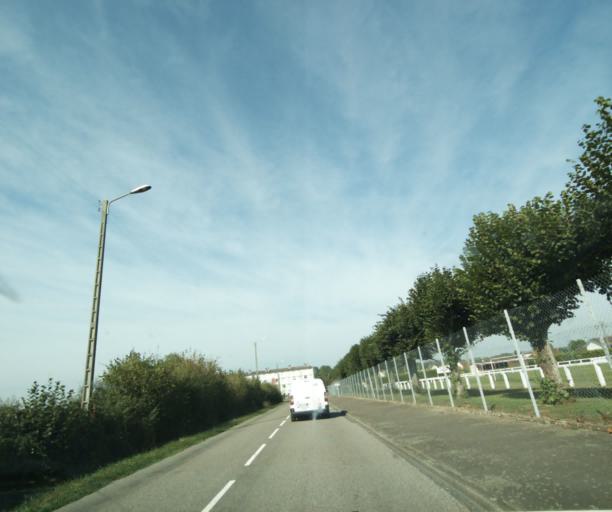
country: FR
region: Bourgogne
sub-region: Departement de Saone-et-Loire
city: Genelard
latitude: 46.5778
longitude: 4.2455
